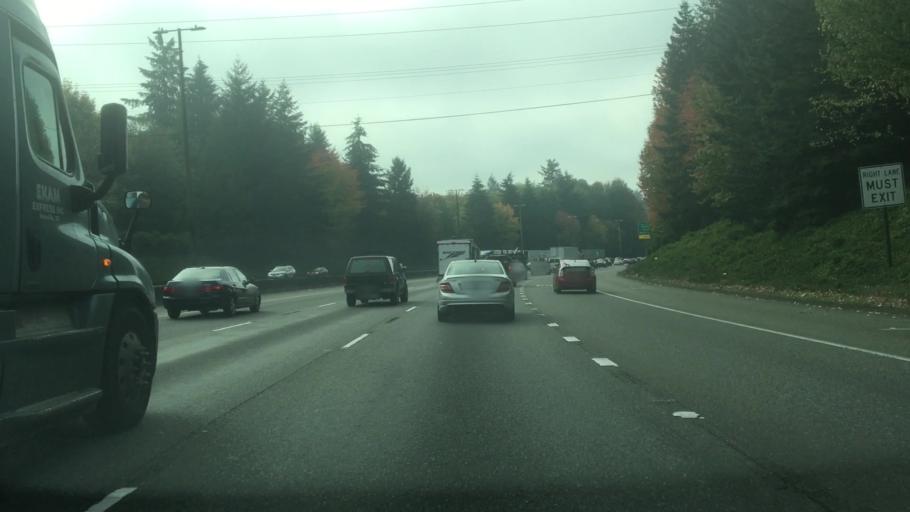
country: US
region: Washington
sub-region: Thurston County
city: Olympia
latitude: 47.0372
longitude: -122.8746
